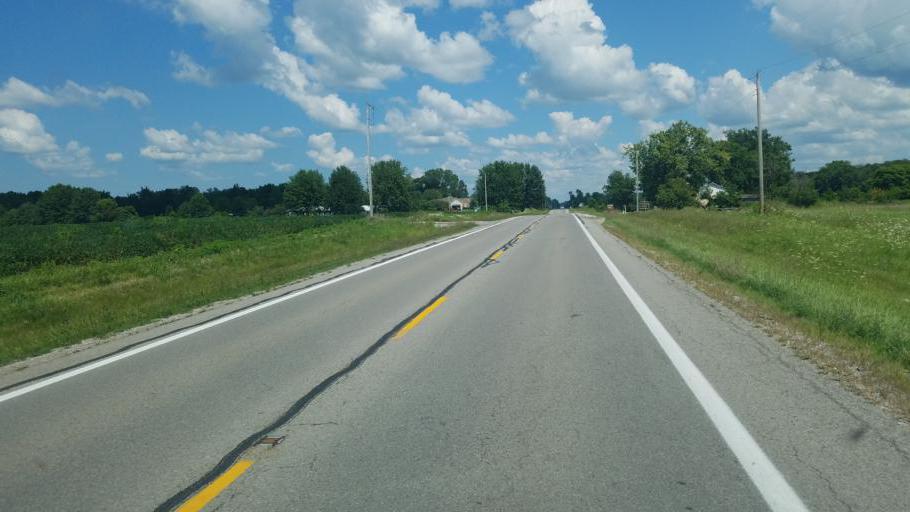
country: US
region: Ohio
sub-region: Morrow County
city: Mount Gilead
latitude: 40.6393
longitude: -82.9317
